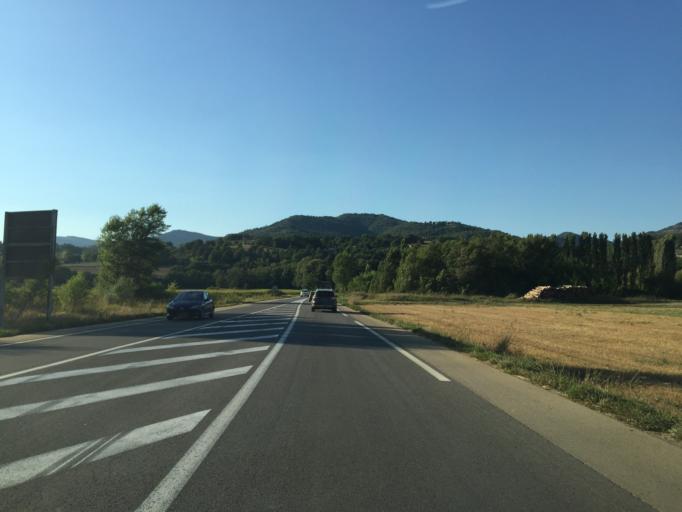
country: FR
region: Provence-Alpes-Cote d'Azur
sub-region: Departement des Alpes-de-Haute-Provence
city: Mallemoisson
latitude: 44.0433
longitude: 6.1397
